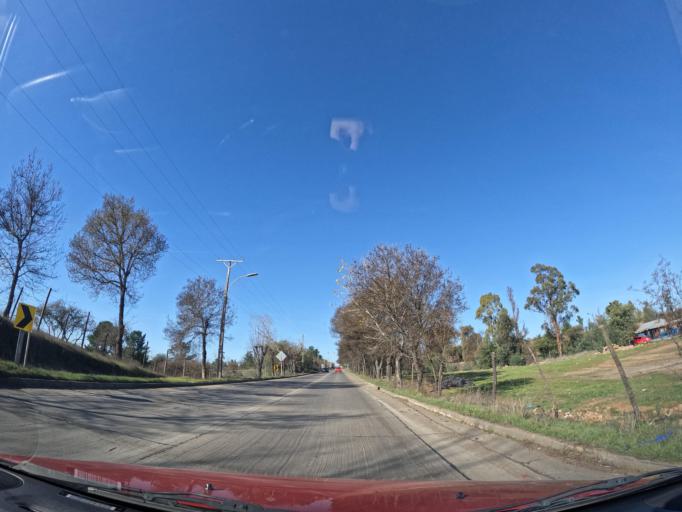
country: CL
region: Maule
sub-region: Provincia de Cauquenes
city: Cauquenes
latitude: -35.9554
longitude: -72.3099
